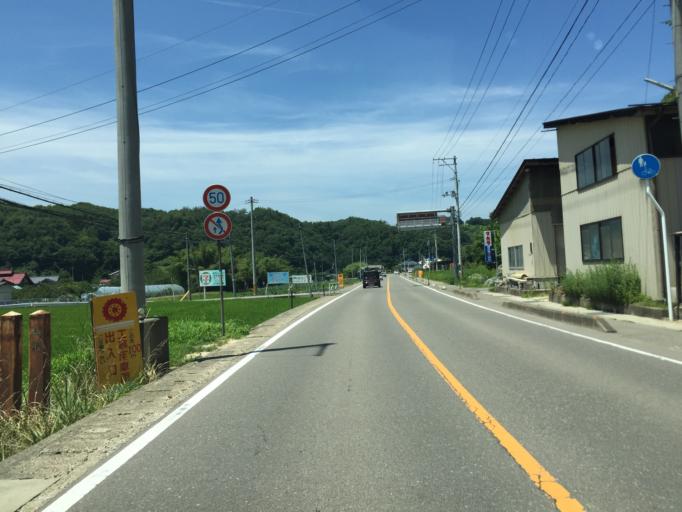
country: JP
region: Fukushima
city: Hobaramachi
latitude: 37.7656
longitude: 140.6141
